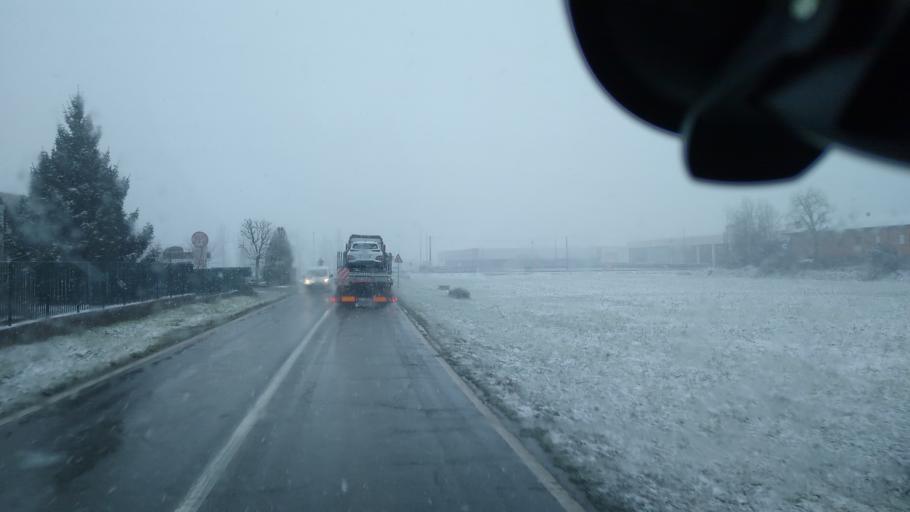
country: IT
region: Lombardy
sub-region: Provincia di Bergamo
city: Bariano
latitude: 45.4963
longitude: 9.6979
